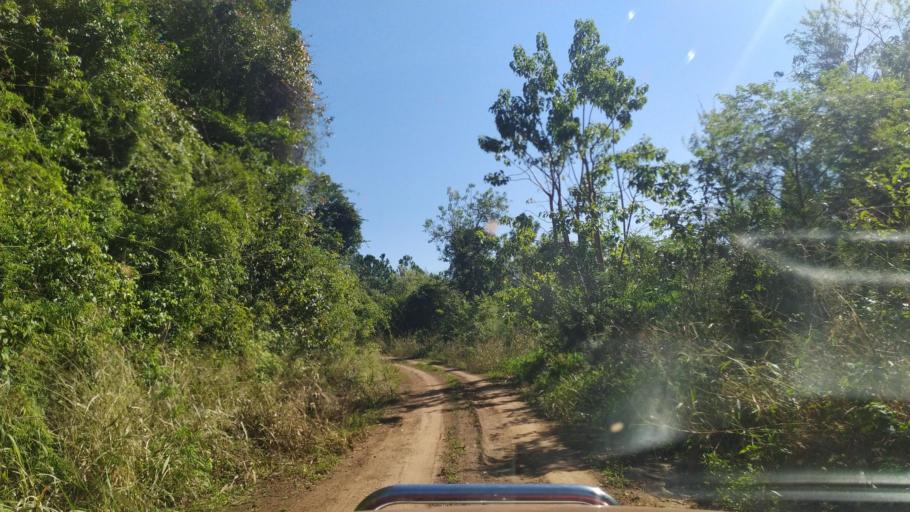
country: AR
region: Misiones
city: El Alcazar
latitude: -26.7587
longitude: -54.5883
